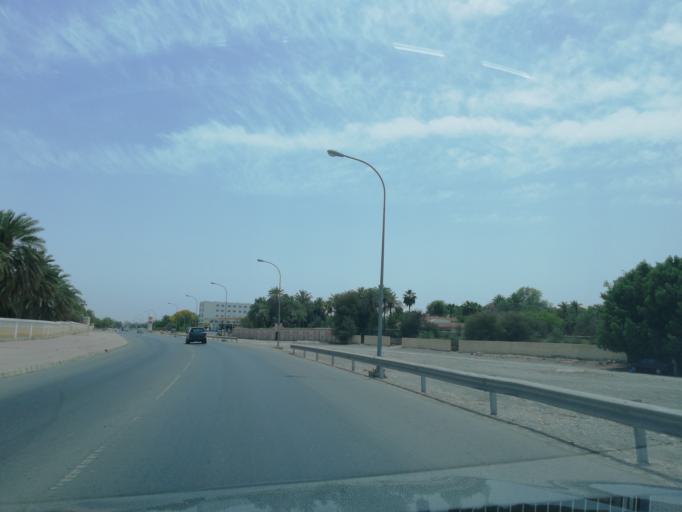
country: OM
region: Muhafazat Masqat
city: As Sib al Jadidah
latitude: 23.6807
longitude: 58.1679
